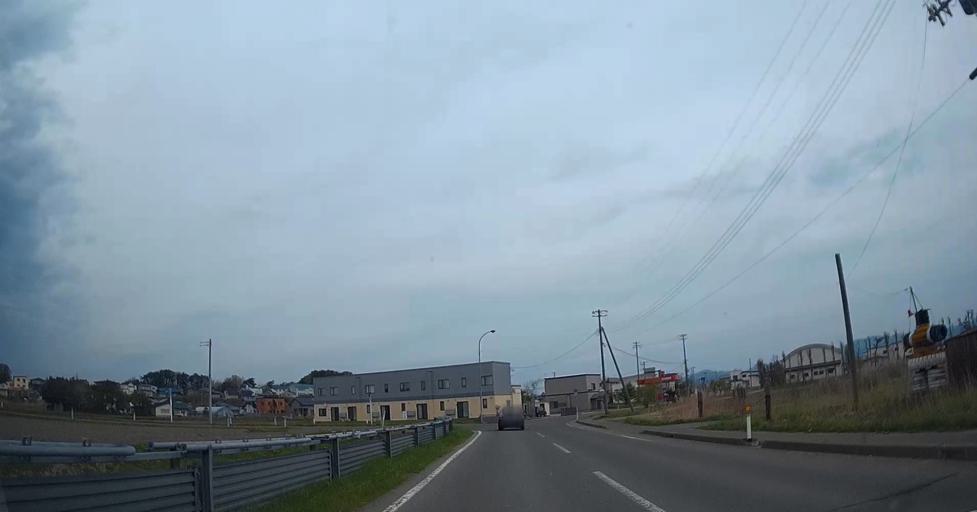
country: JP
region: Aomori
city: Shimokizukuri
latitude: 40.9767
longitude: 140.3703
